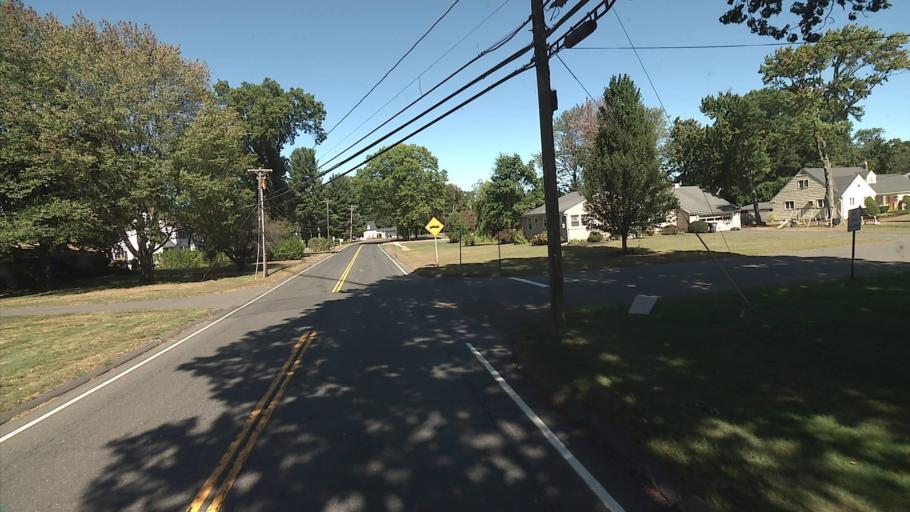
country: US
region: Connecticut
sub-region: New Haven County
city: Cheshire Village
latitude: 41.5685
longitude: -72.8991
